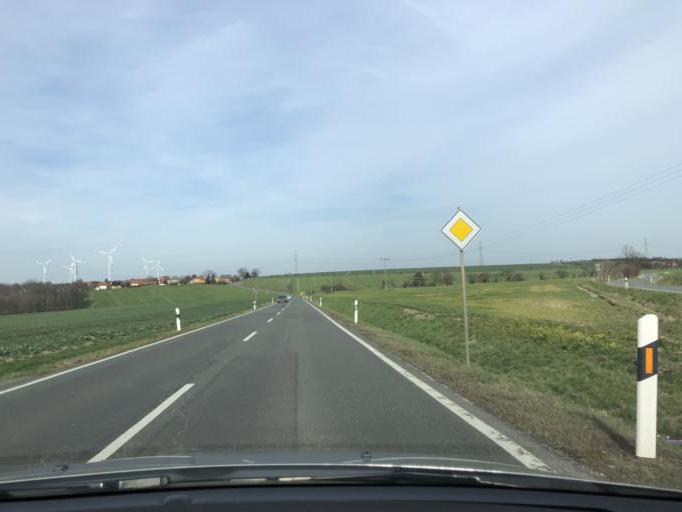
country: DE
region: Thuringia
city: Walpernhain
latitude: 51.0106
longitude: 11.9190
